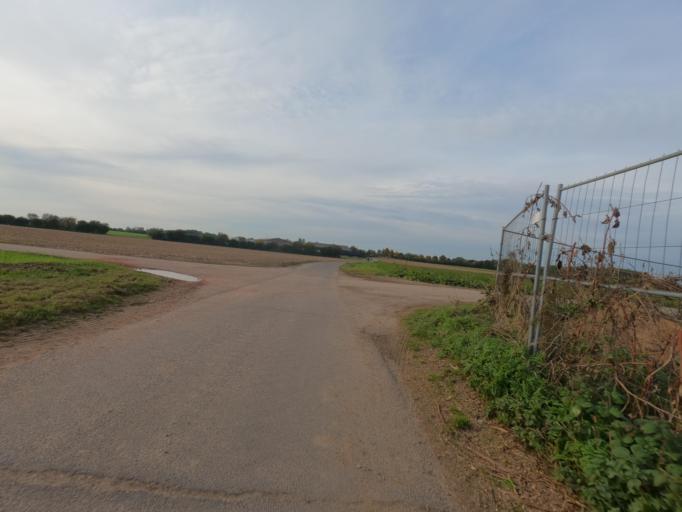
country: DE
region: North Rhine-Westphalia
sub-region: Regierungsbezirk Koln
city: Wassenberg
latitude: 51.0357
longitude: 6.1611
